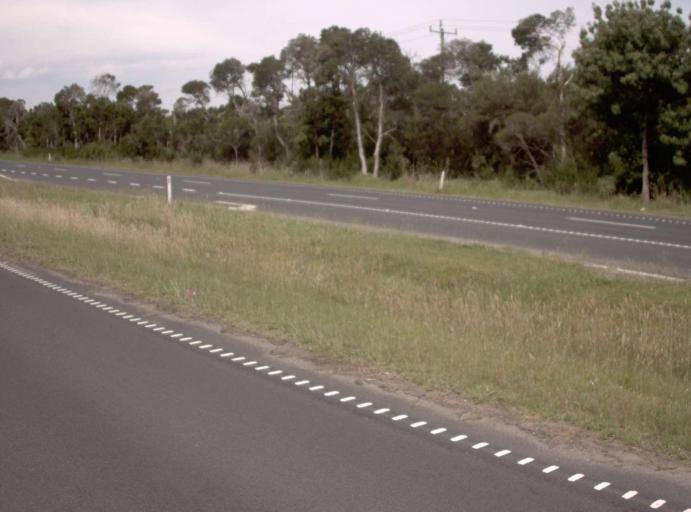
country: AU
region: Victoria
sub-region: Mornington Peninsula
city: Moorooduc
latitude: -38.2049
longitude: 145.1181
